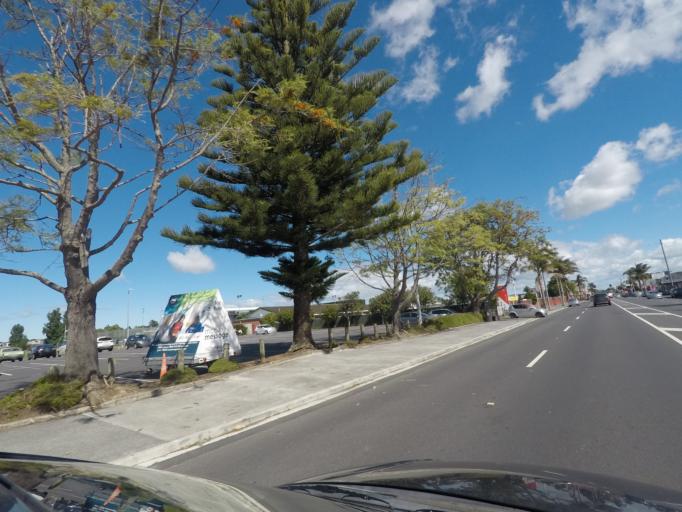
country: NZ
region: Auckland
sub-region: Auckland
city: Wiri
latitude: -36.9725
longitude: 174.8633
